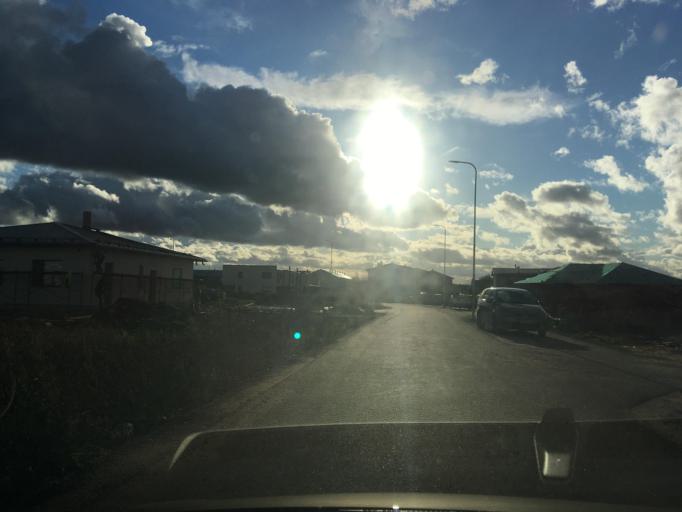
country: EE
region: Harju
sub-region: Joelaehtme vald
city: Loo
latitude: 59.4436
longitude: 24.9651
